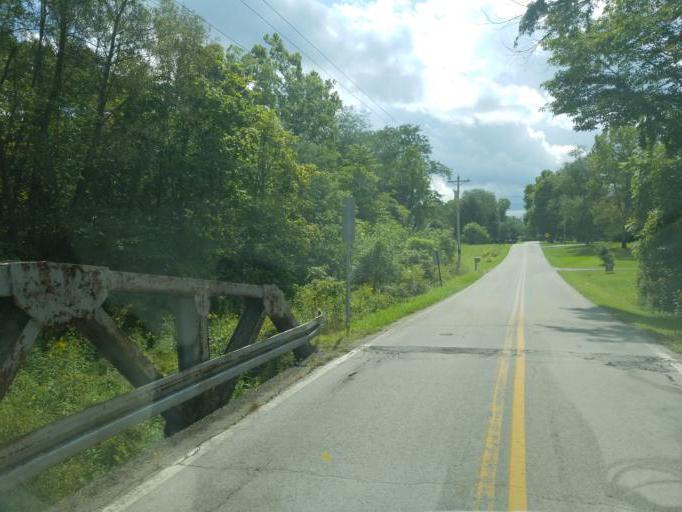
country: US
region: Ohio
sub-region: Huron County
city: Norwalk
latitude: 41.1558
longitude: -82.6342
